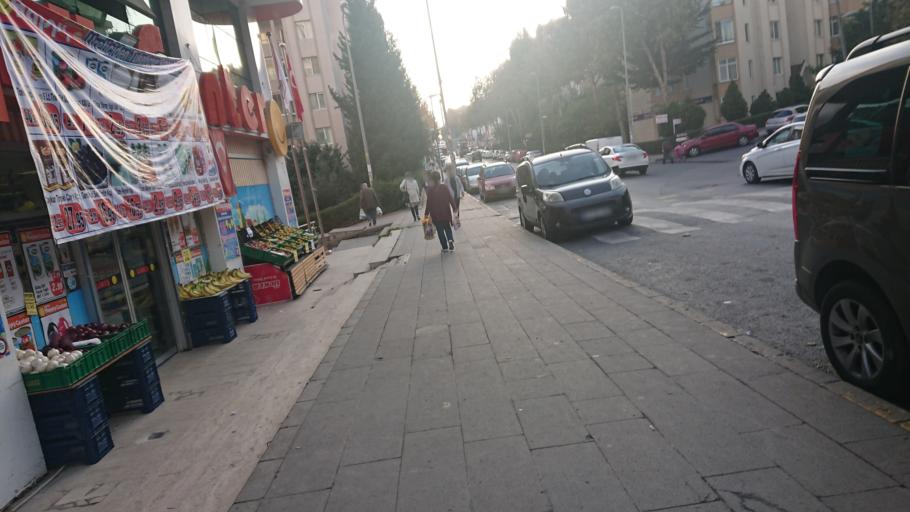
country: TR
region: Istanbul
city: Esenyurt
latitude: 41.0620
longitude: 28.6786
